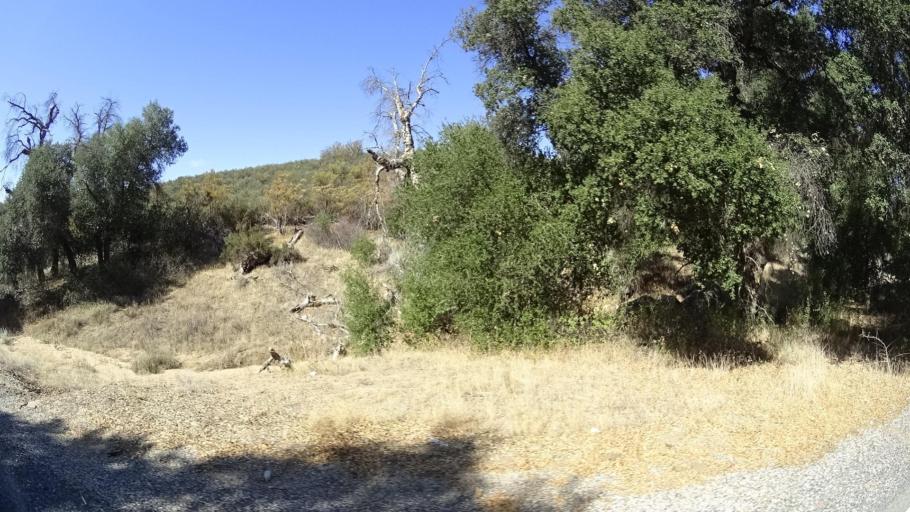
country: US
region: California
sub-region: Riverside County
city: Aguanga
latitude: 33.3250
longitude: -116.7019
